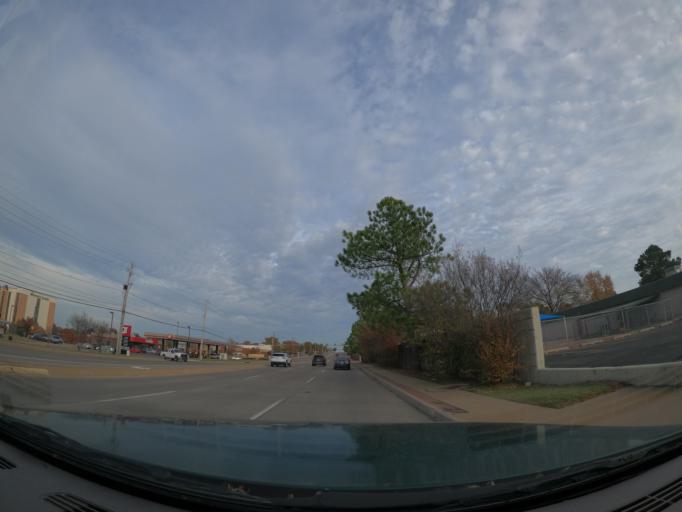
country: US
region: Oklahoma
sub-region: Tulsa County
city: Jenks
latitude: 36.0607
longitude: -95.9202
